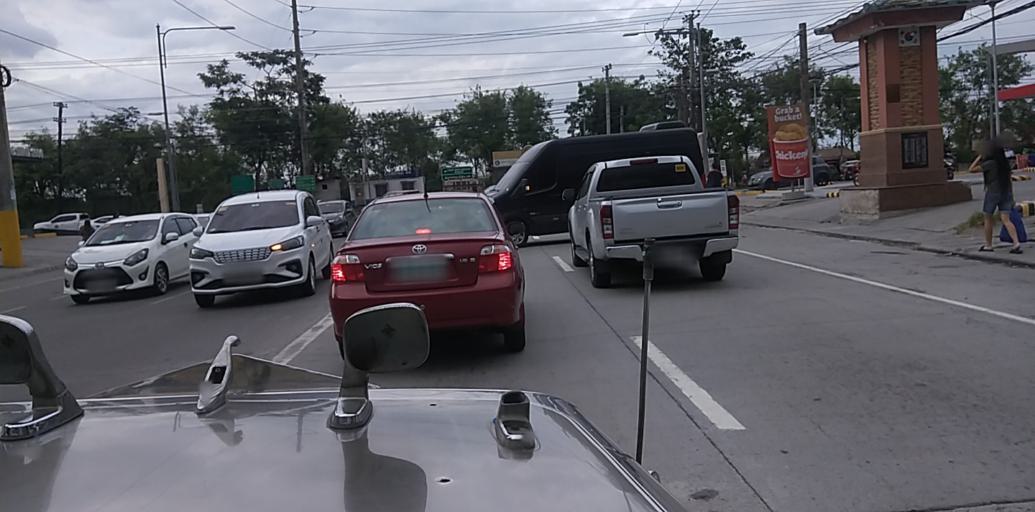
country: PH
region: Central Luzon
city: Santol
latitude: 15.1626
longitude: 120.5550
